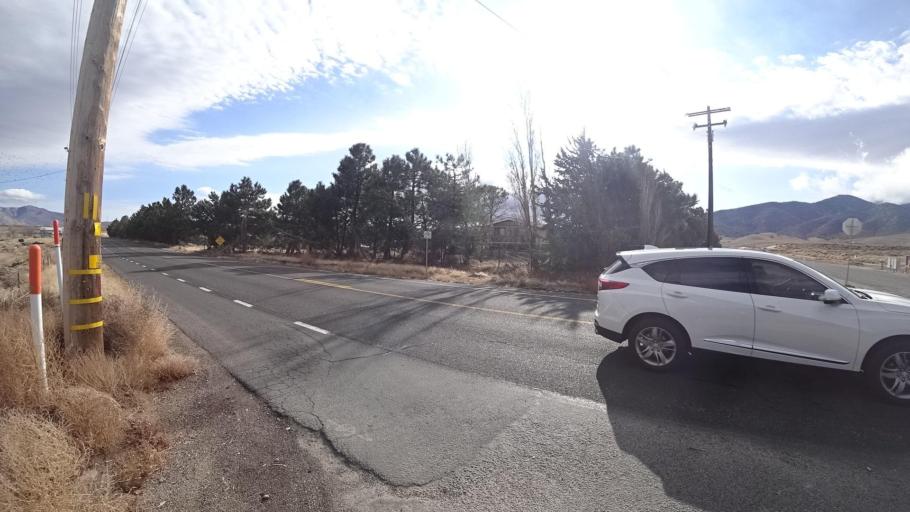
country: US
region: California
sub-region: Kern County
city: Tehachapi
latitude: 35.1097
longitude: -118.4323
